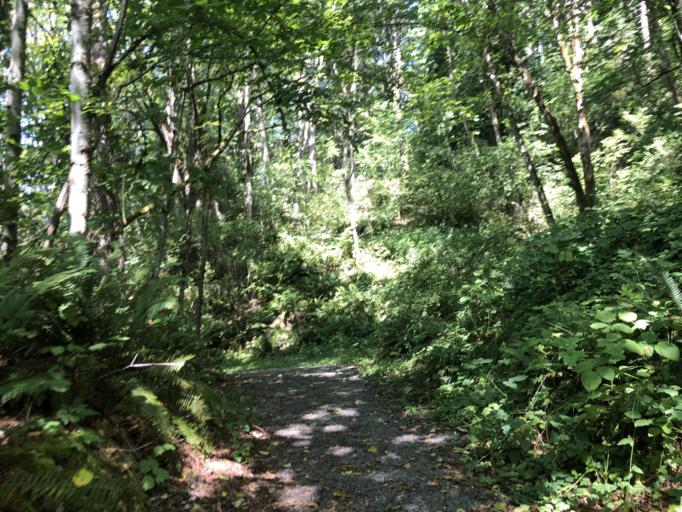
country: US
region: Washington
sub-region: King County
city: Lea Hill
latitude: 47.3449
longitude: -122.2054
